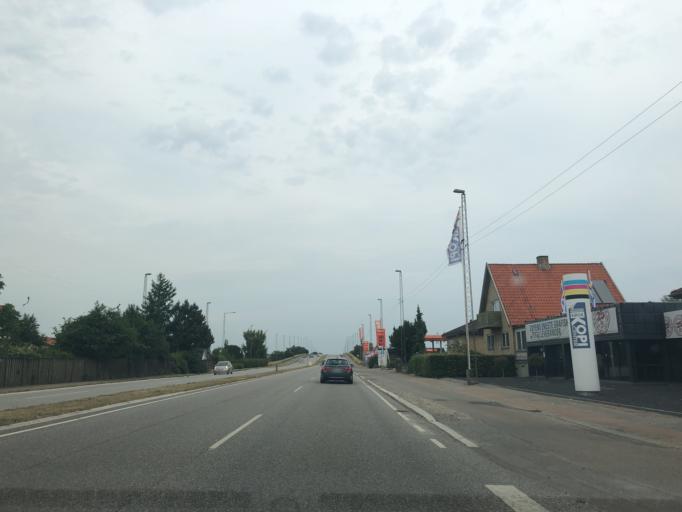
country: DK
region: Zealand
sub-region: Koge Kommune
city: Koge
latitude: 55.4702
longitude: 12.1809
